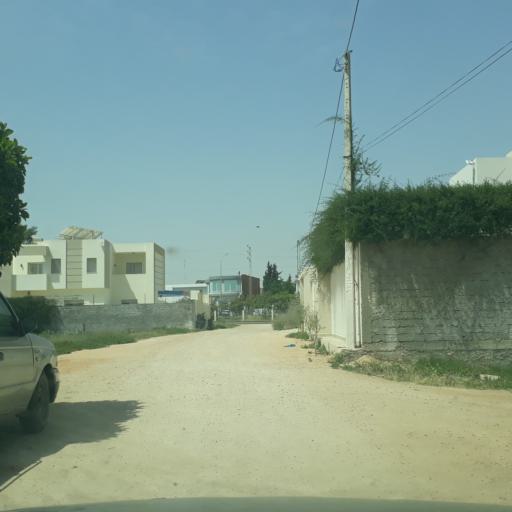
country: TN
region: Safaqis
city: Al Qarmadah
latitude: 34.7945
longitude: 10.7616
